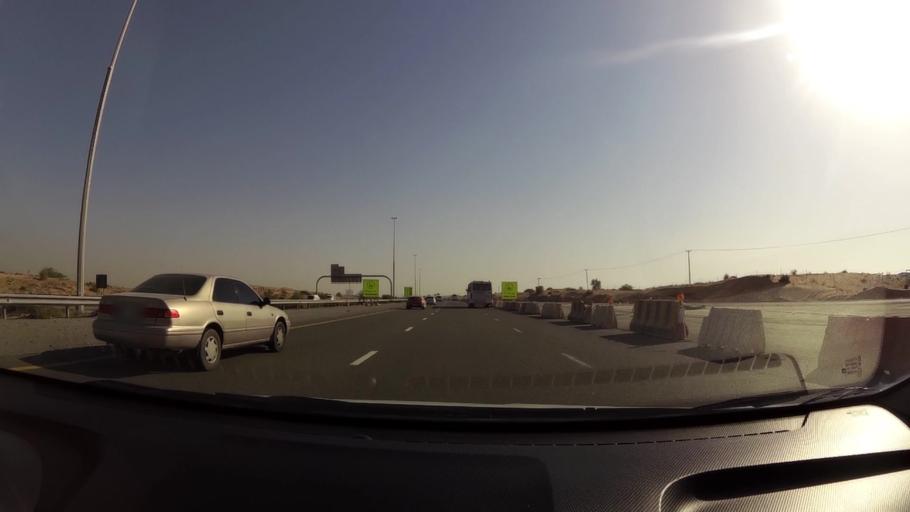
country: AE
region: Umm al Qaywayn
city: Umm al Qaywayn
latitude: 25.4383
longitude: 55.6006
